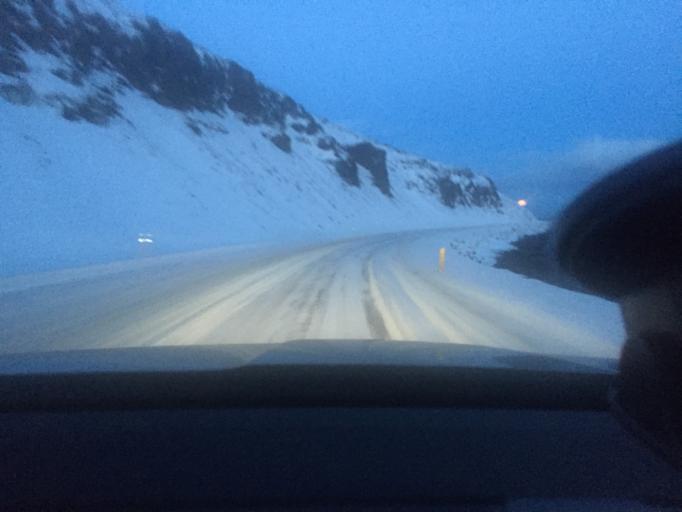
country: IS
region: Westfjords
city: Isafjoerdur
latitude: 66.0954
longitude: -23.0279
